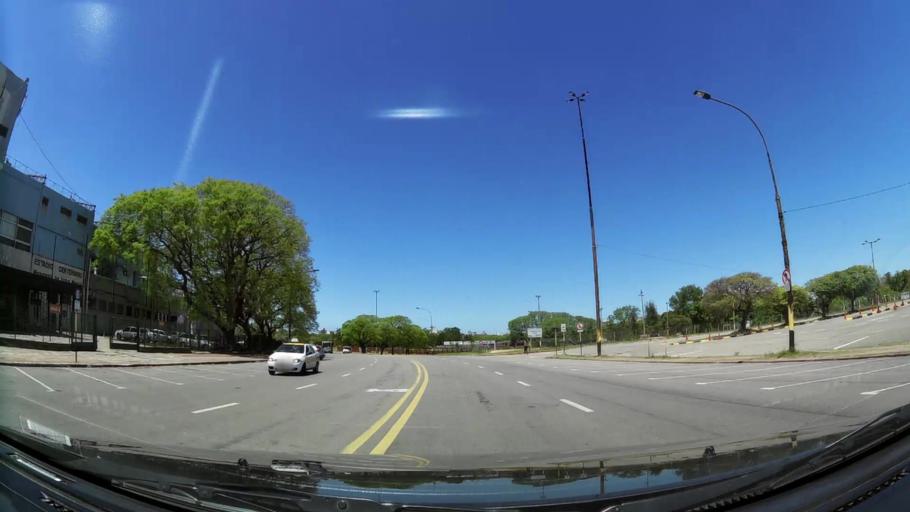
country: UY
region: Montevideo
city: Montevideo
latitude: -34.8950
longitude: -56.1543
